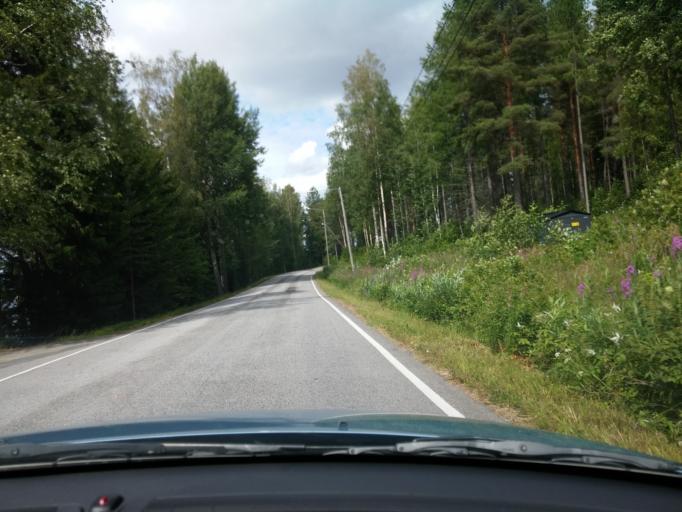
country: FI
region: Central Finland
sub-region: Saarijaervi-Viitasaari
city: Saarijaervi
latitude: 62.7214
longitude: 25.1981
